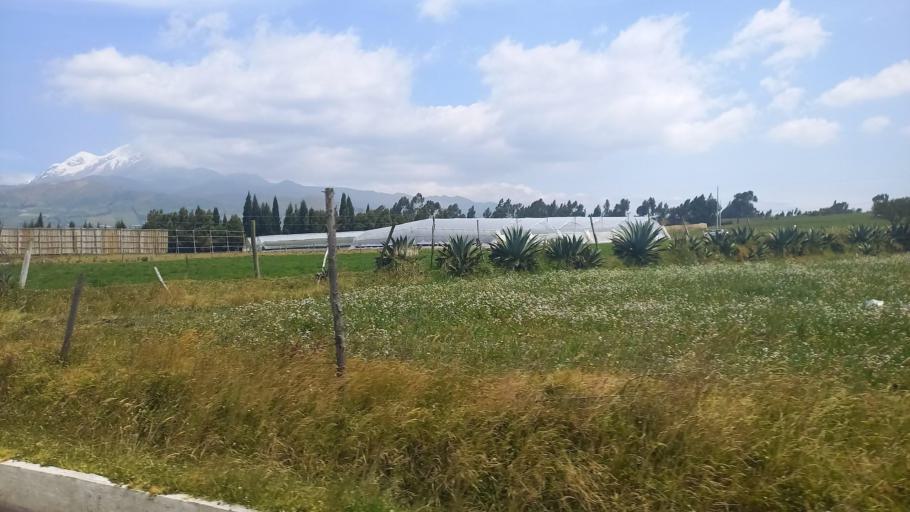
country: EC
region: Pichincha
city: Cayambe
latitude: 0.1620
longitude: -78.0812
